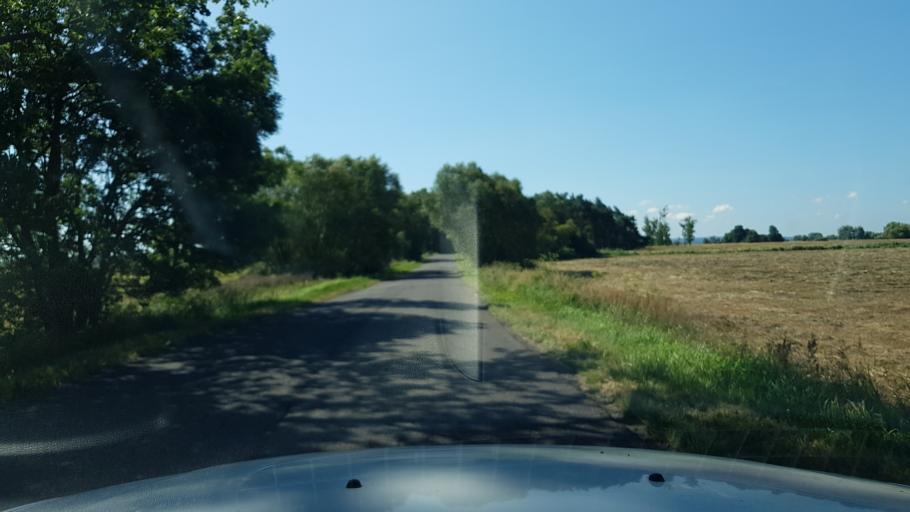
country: PL
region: West Pomeranian Voivodeship
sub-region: Powiat goleniowski
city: Goleniow
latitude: 53.4860
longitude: 14.7117
